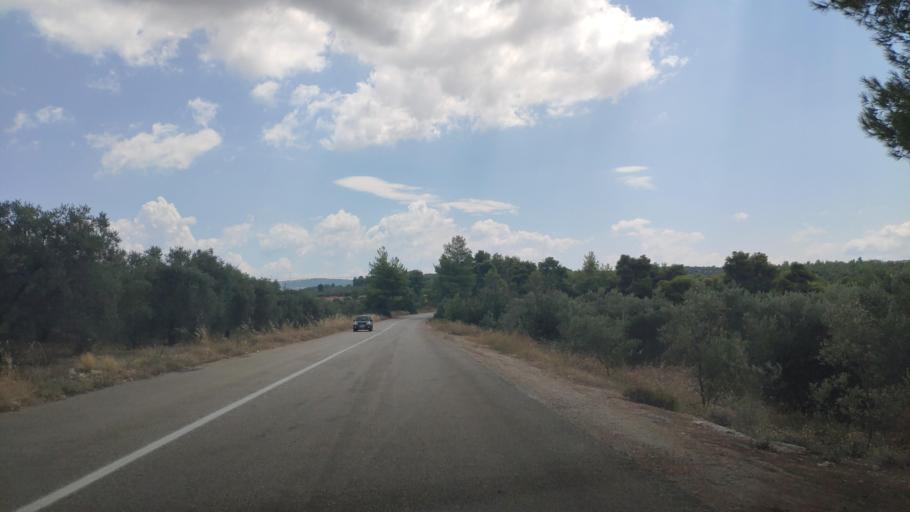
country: GR
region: Central Greece
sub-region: Nomos Fthiotidos
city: Malesina
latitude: 38.6291
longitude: 23.1769
